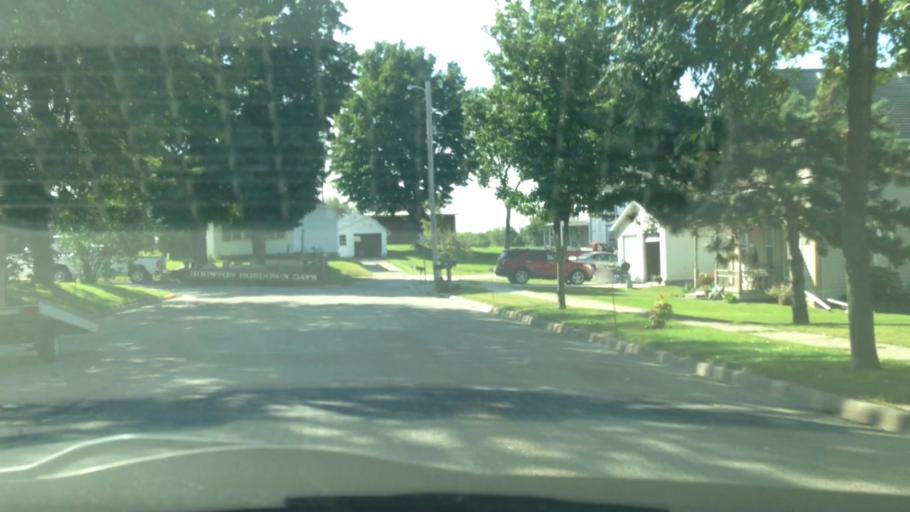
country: US
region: Minnesota
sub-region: Houston County
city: Spring Grove
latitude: 43.5209
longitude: -91.7744
